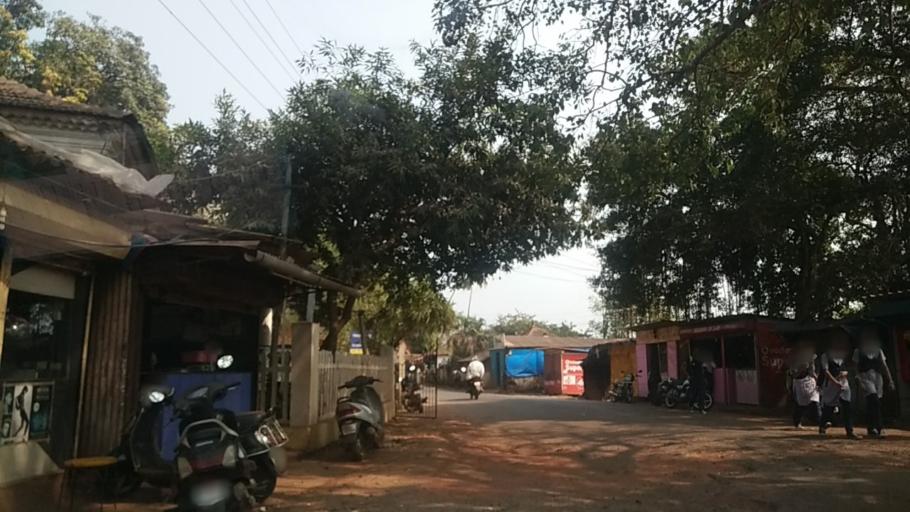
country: IN
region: Goa
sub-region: North Goa
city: Panaji
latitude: 15.5061
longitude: 73.8260
